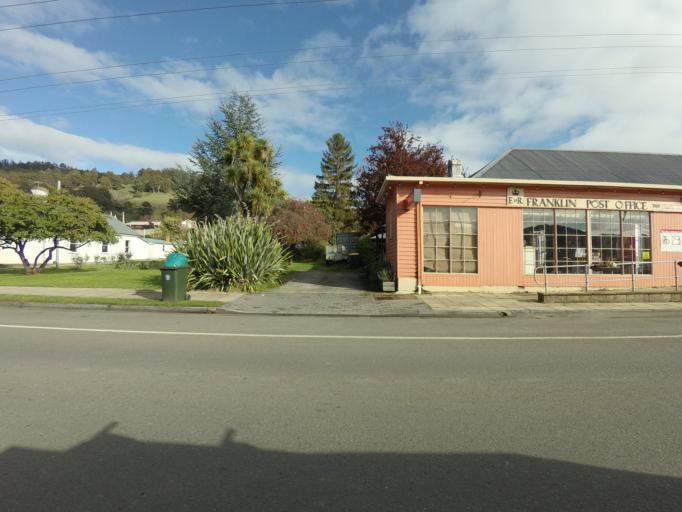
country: AU
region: Tasmania
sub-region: Huon Valley
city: Franklin
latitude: -43.0902
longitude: 147.0102
